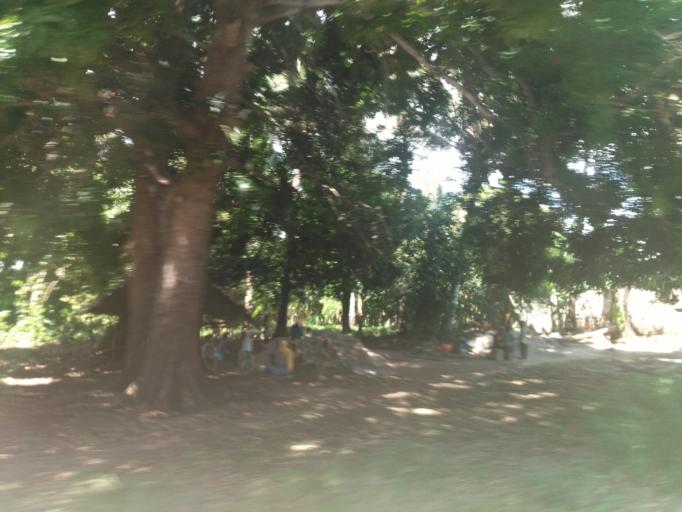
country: TZ
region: Zanzibar North
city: Gamba
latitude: -5.9352
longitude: 39.3414
